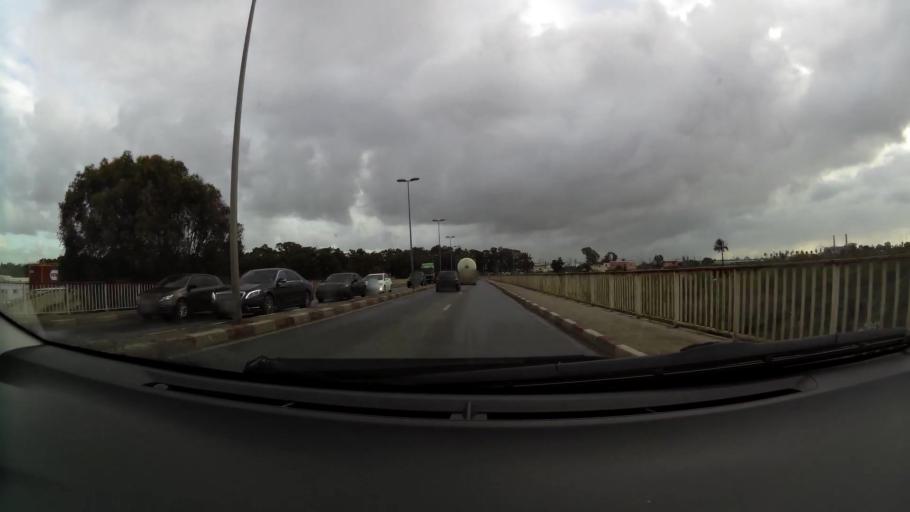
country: MA
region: Grand Casablanca
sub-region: Mohammedia
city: Mohammedia
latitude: 33.6795
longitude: -7.4103
